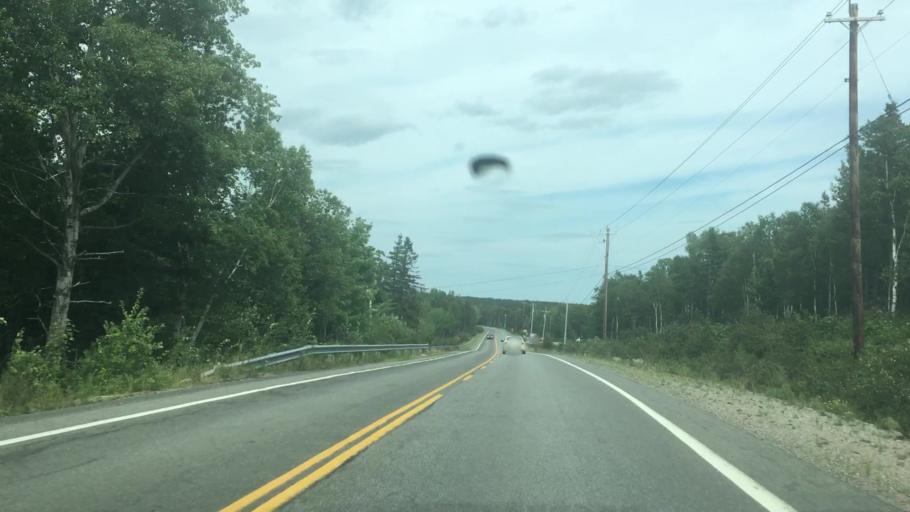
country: CA
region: Nova Scotia
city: Sydney Mines
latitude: 46.5047
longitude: -60.4349
